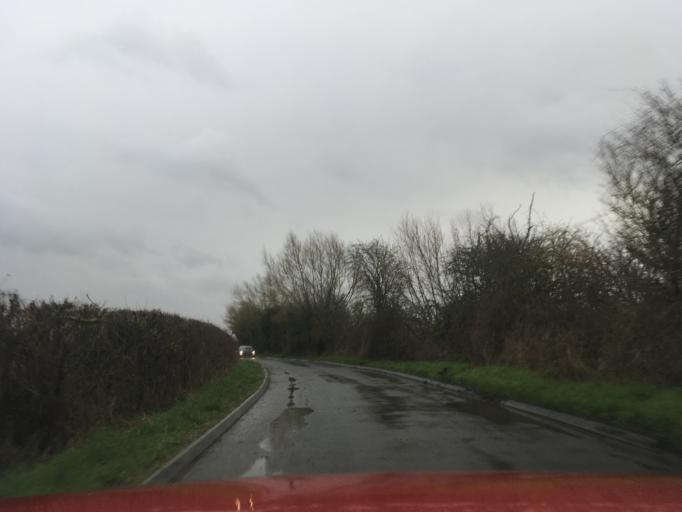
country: GB
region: England
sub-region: Oxfordshire
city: Oxford
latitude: 51.7589
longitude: -1.2856
